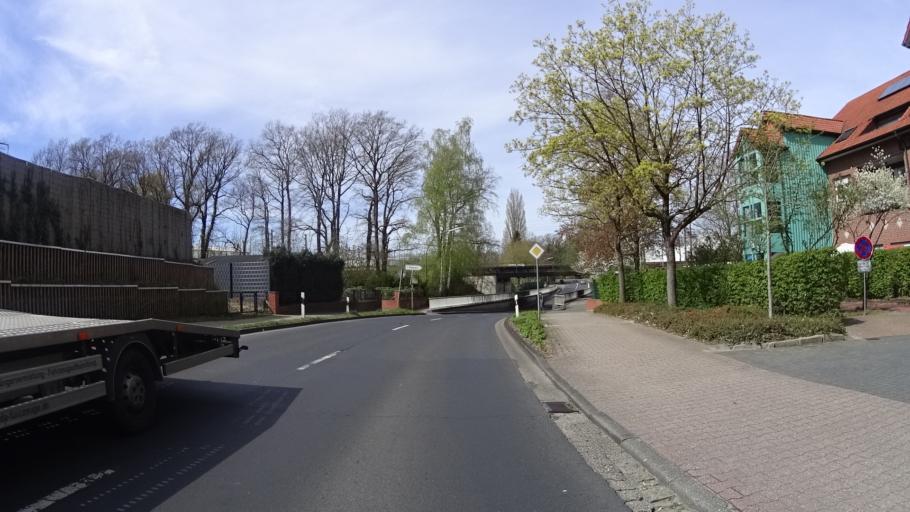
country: DE
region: Lower Saxony
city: Lingen
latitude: 52.5020
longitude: 7.3103
